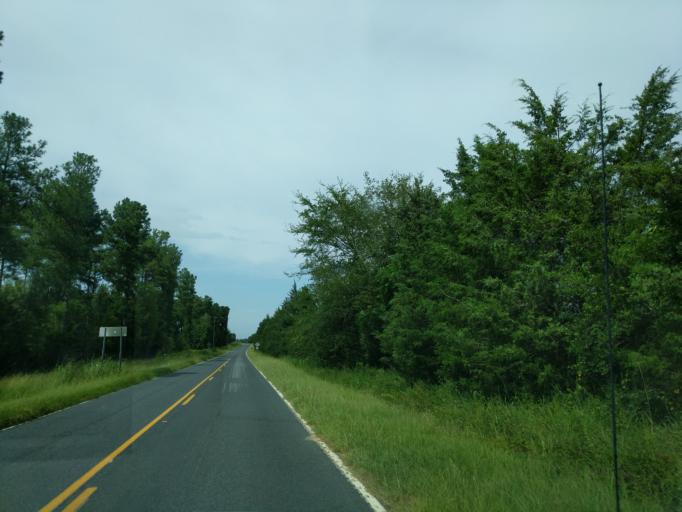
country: US
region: South Carolina
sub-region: Abbeville County
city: Lake Secession
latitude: 34.2552
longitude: -82.5601
